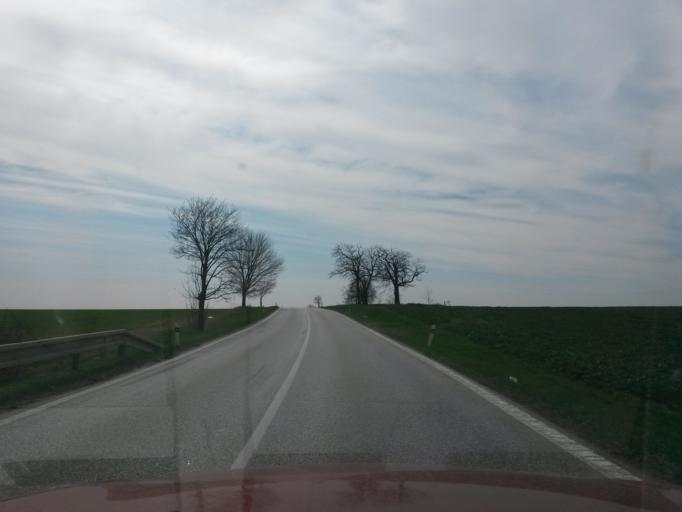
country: SK
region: Nitriansky
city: Svodin
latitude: 48.0103
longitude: 18.3799
